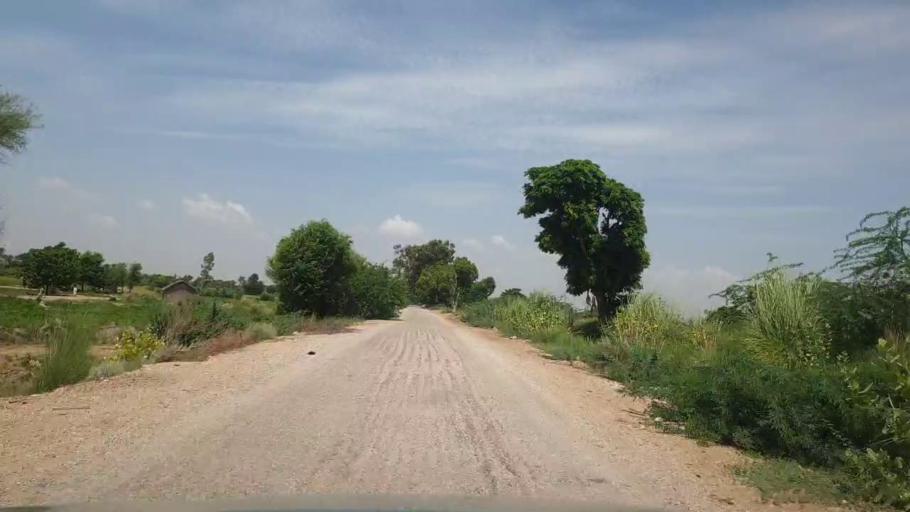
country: PK
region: Sindh
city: Bozdar
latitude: 27.0831
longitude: 68.9774
